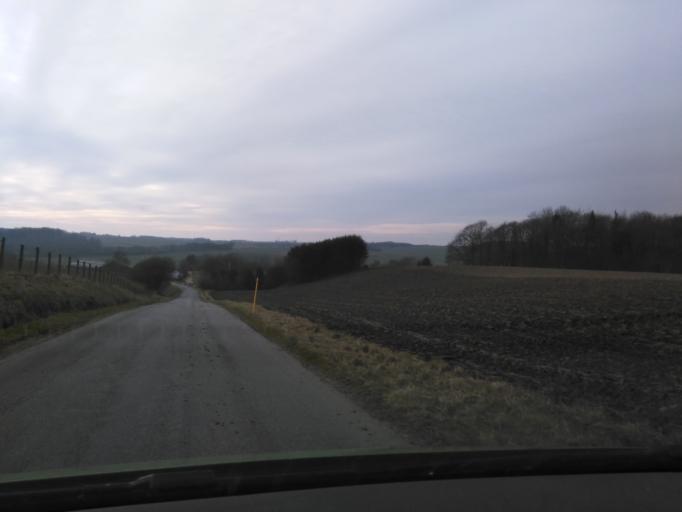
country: DK
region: Central Jutland
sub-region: Odder Kommune
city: Odder
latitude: 55.9274
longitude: 10.1189
